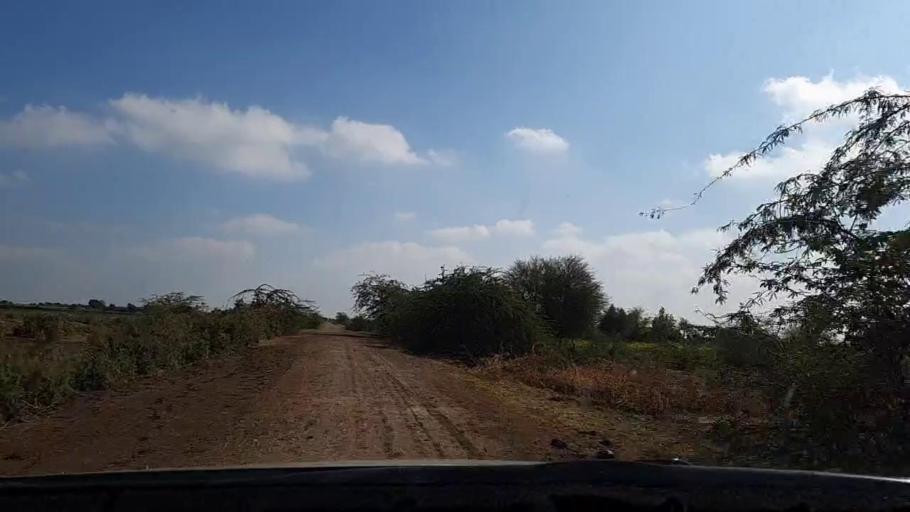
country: PK
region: Sindh
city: Pithoro
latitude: 25.7267
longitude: 69.2893
